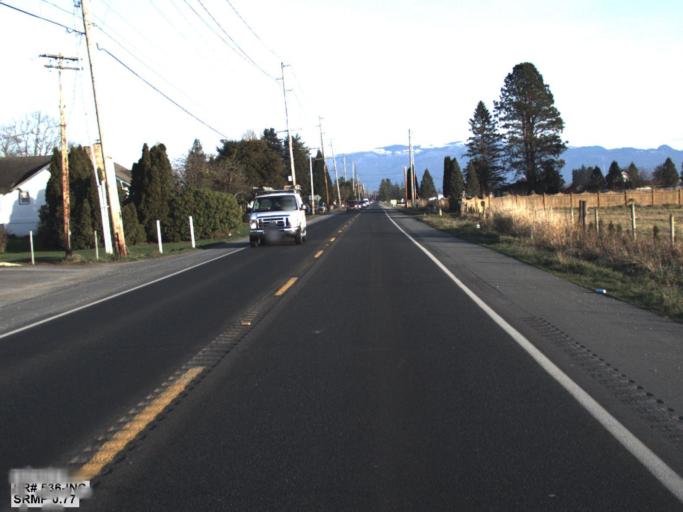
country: US
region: Washington
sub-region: Skagit County
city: Mount Vernon
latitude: 48.4428
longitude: -122.4159
